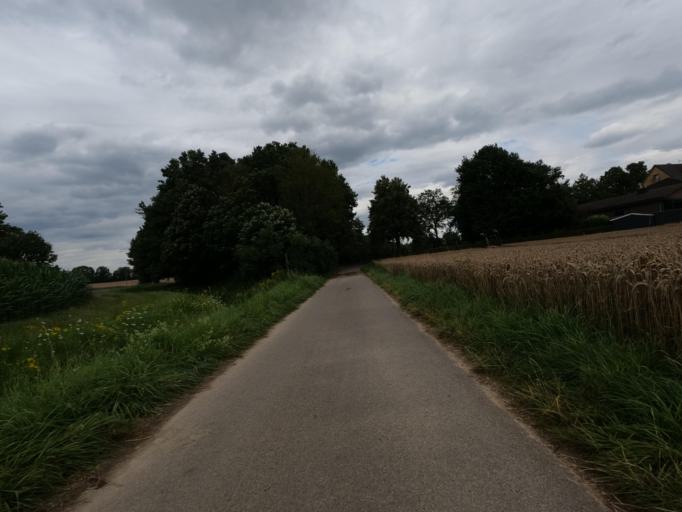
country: DE
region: North Rhine-Westphalia
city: Geilenkirchen
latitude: 50.9868
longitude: 6.1805
